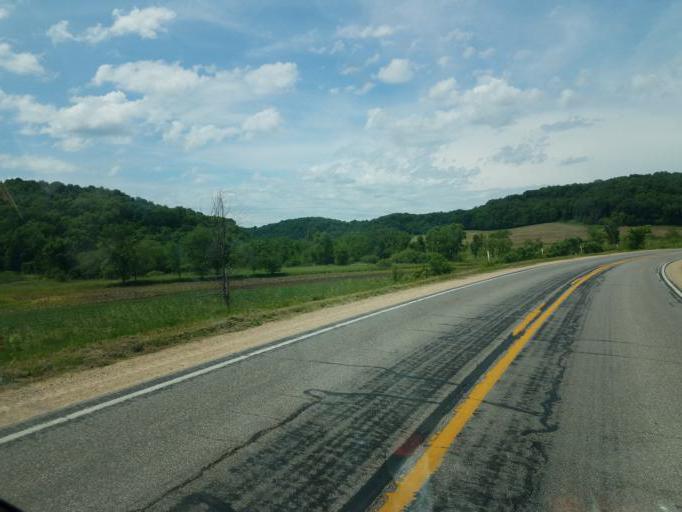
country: US
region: Wisconsin
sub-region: Vernon County
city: Hillsboro
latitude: 43.6442
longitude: -90.4114
